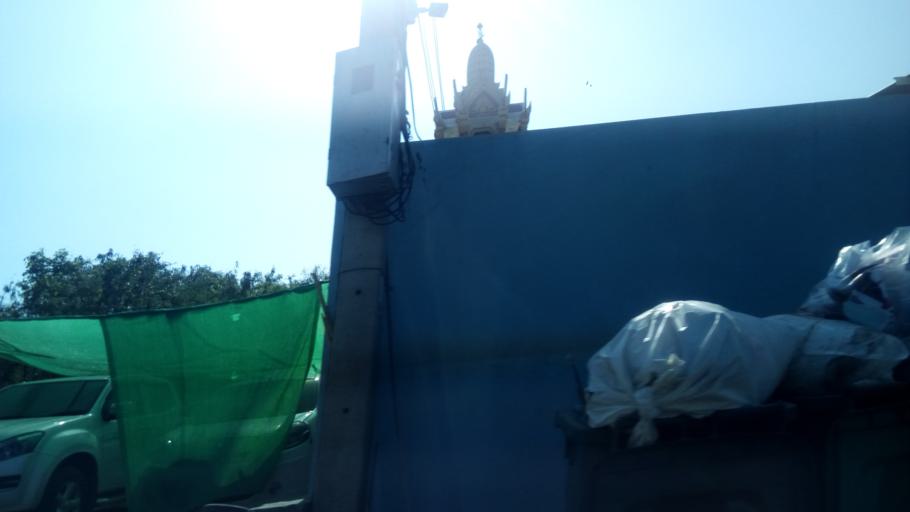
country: TH
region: Nakhon Pathom
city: Salaya
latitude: 13.8093
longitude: 100.3091
